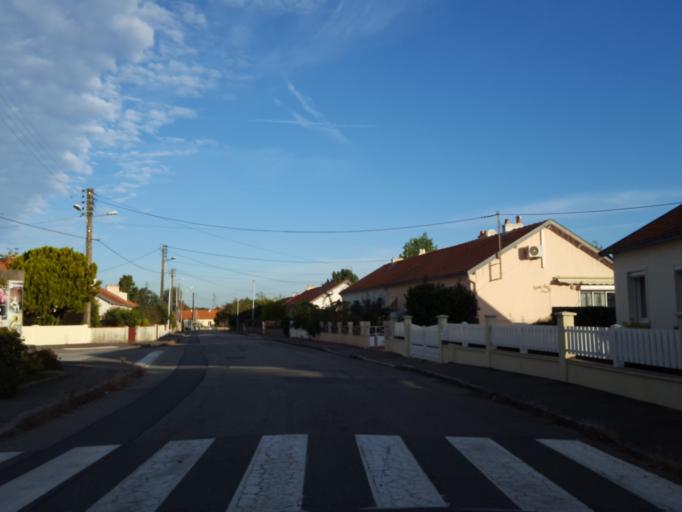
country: FR
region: Pays de la Loire
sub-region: Departement de la Loire-Atlantique
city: Saint-Sebastien-sur-Loire
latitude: 47.1983
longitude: -1.4872
